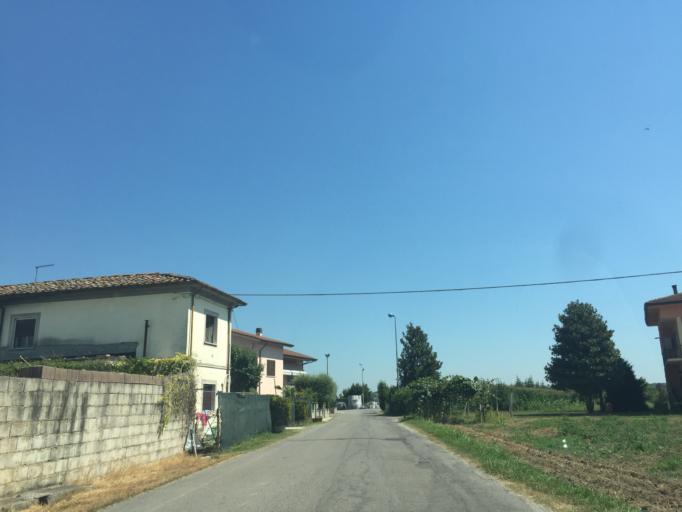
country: IT
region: Tuscany
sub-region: Provincia di Pistoia
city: Anchione
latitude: 43.8212
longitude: 10.7568
